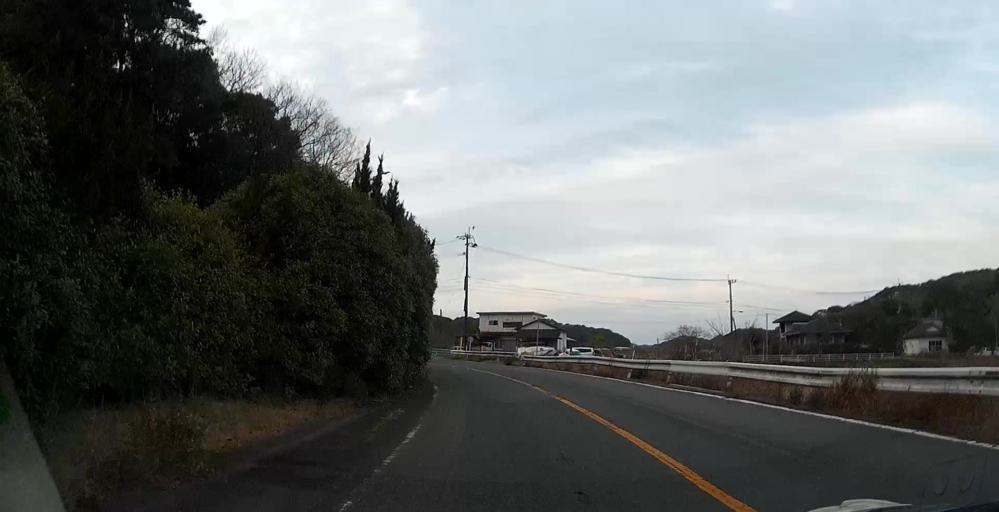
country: JP
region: Kumamoto
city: Hondo
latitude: 32.5082
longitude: 130.3825
